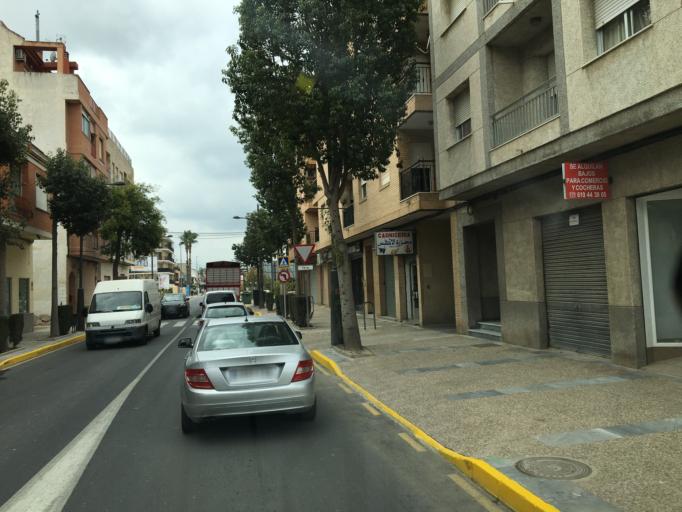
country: ES
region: Murcia
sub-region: Murcia
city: Beniel
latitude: 38.0443
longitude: -1.0039
